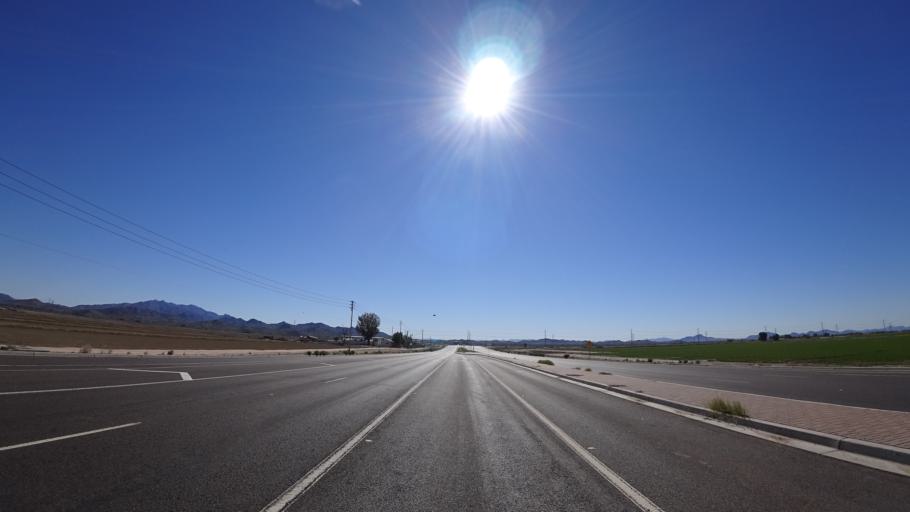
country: US
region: Arizona
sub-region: Maricopa County
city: Goodyear
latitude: 33.4040
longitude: -112.4268
